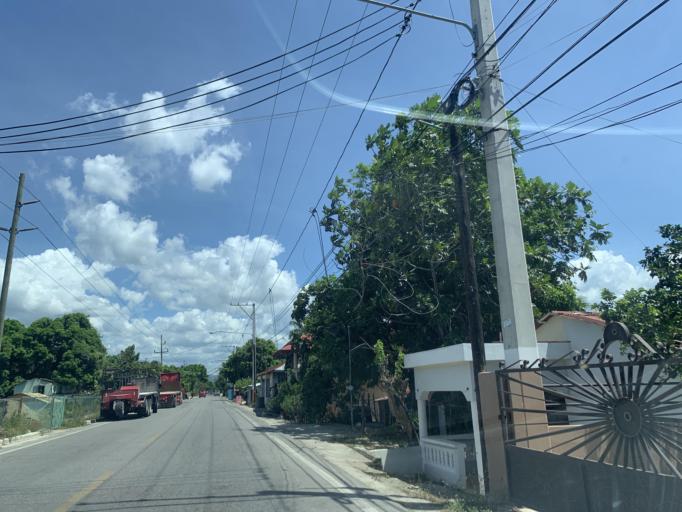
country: DO
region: Puerto Plata
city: Cabarete
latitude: 19.7094
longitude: -70.3846
